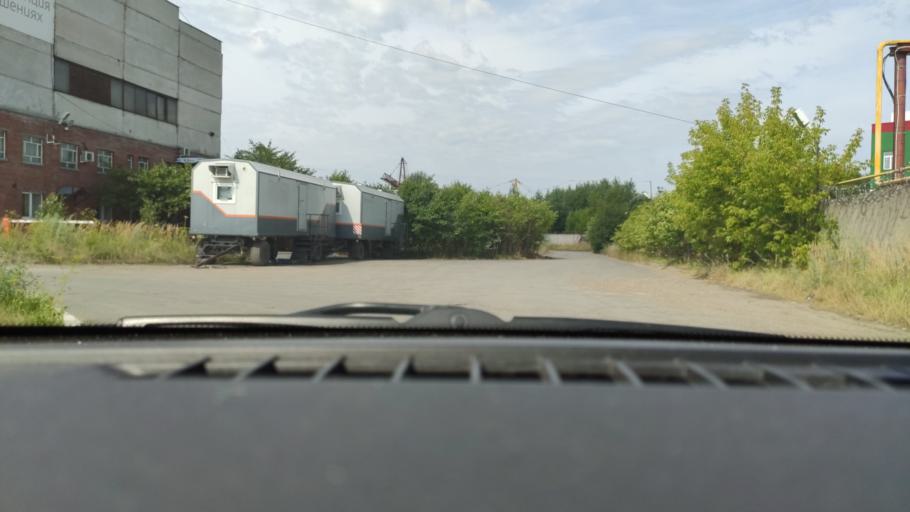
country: RU
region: Perm
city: Kondratovo
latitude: 58.0077
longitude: 56.1483
